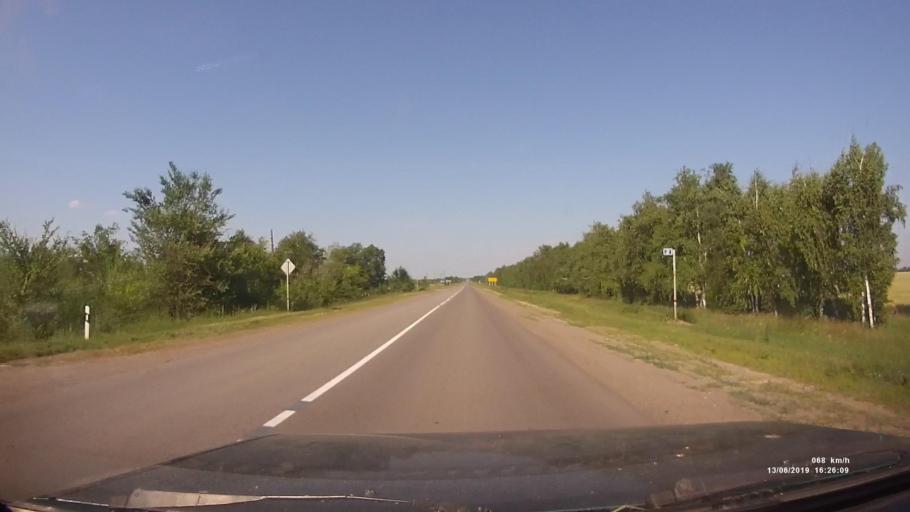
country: RU
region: Rostov
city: Kazanskaya
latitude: 49.8031
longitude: 41.1617
